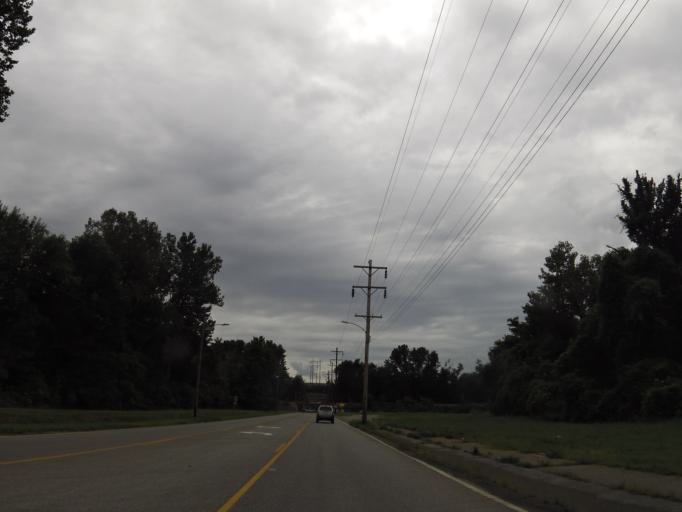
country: US
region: Illinois
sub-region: Alexander County
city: Cairo
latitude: 37.0242
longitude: -89.1862
